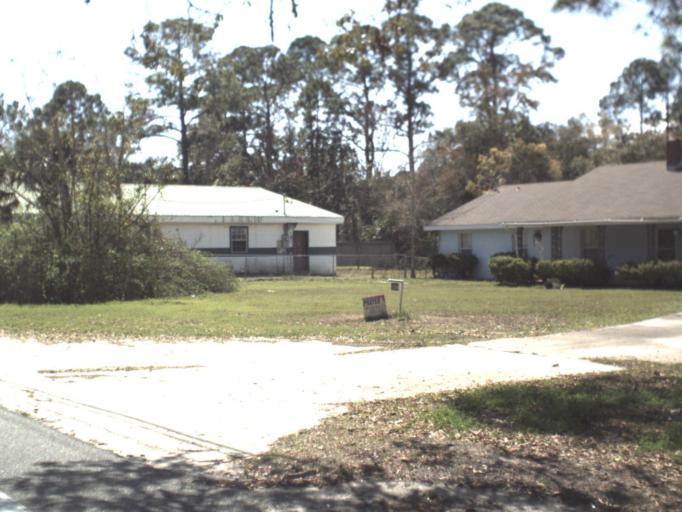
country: US
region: Florida
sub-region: Wakulla County
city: Crawfordville
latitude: 30.0310
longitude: -84.3905
